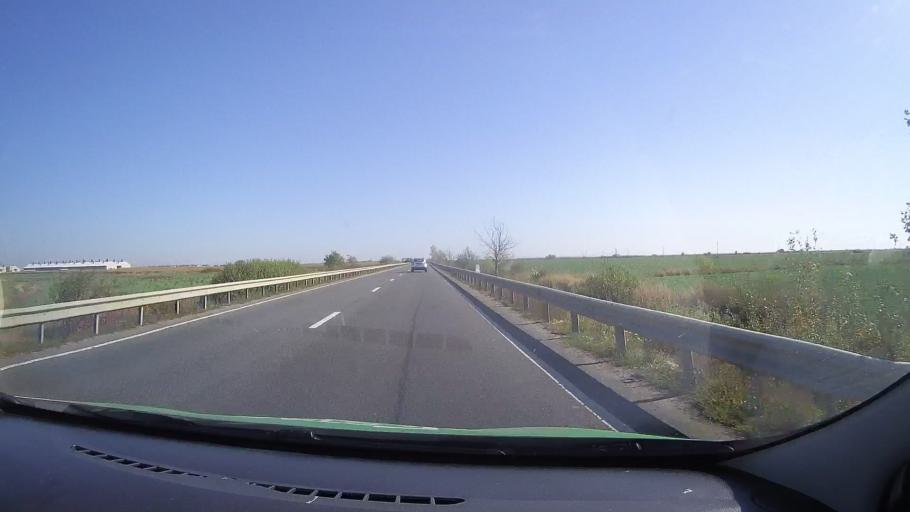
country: RO
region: Satu Mare
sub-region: Comuna Moftinu
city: Domanesti
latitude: 47.6850
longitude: 22.5453
